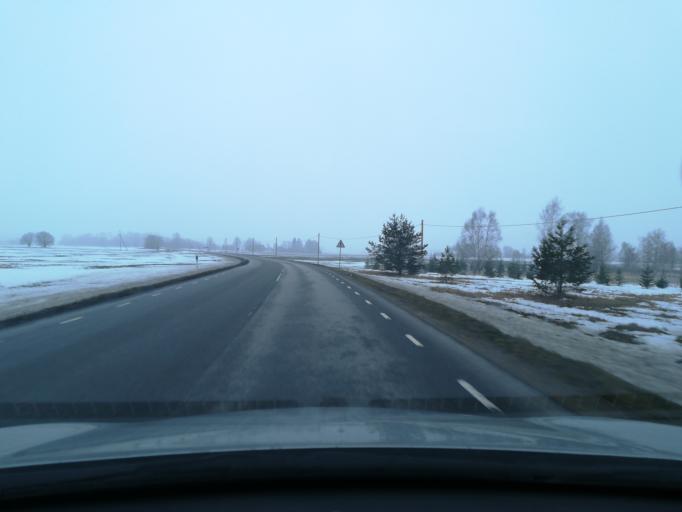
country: EE
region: Harju
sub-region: Raasiku vald
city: Raasiku
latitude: 59.3553
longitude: 25.1460
